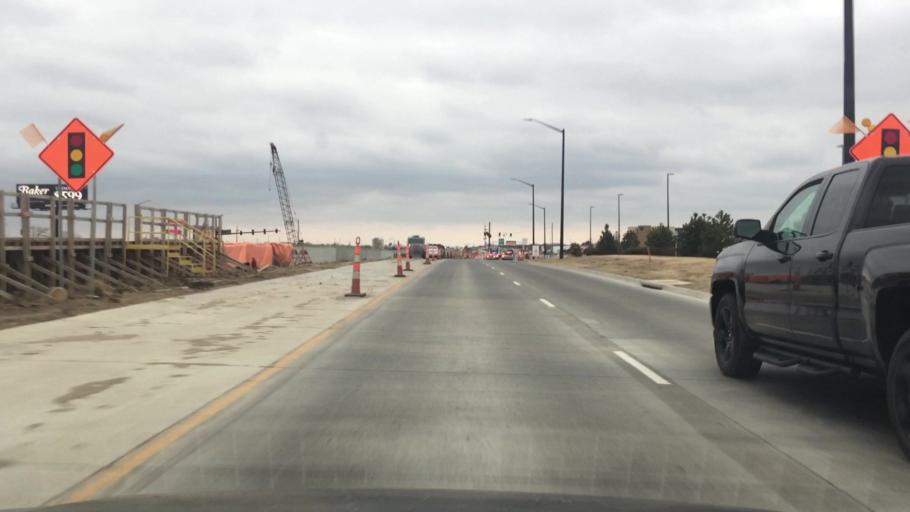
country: US
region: Kansas
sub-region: Butler County
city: Andover
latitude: 37.6794
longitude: -97.2229
